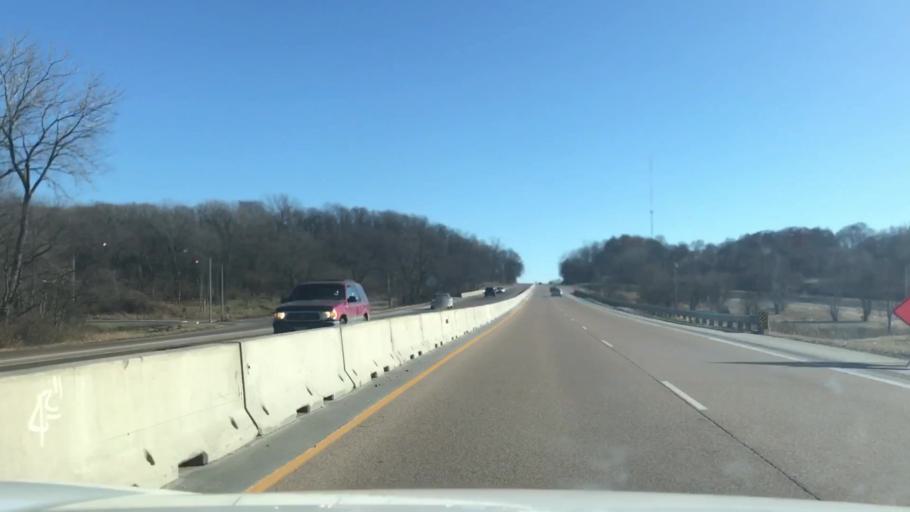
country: US
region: Illinois
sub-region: Saint Clair County
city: Alorton
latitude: 38.5687
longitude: -90.0926
